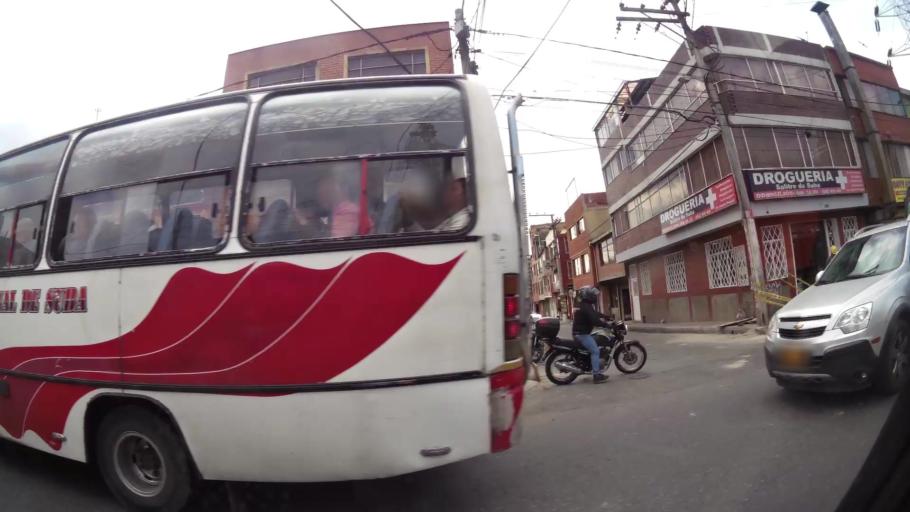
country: CO
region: Cundinamarca
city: Cota
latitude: 4.7563
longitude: -74.0797
